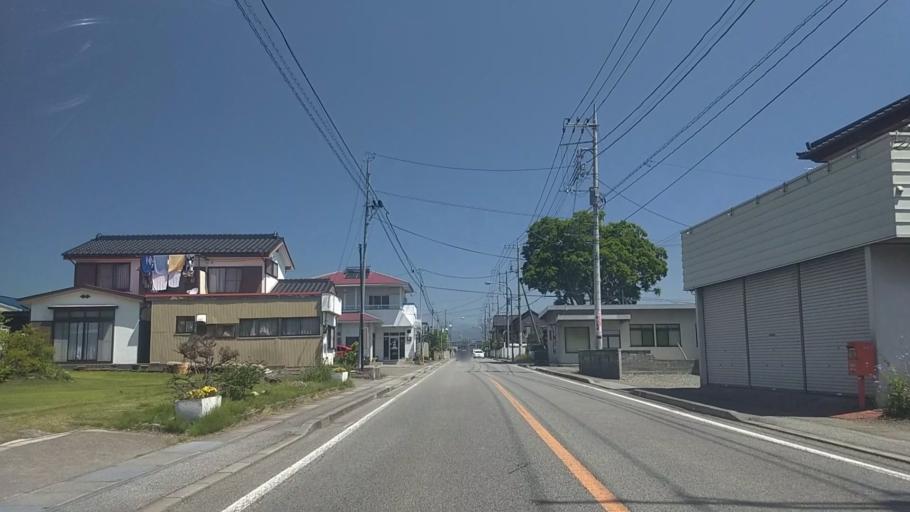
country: JP
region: Yamanashi
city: Ryuo
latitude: 35.6514
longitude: 138.4635
